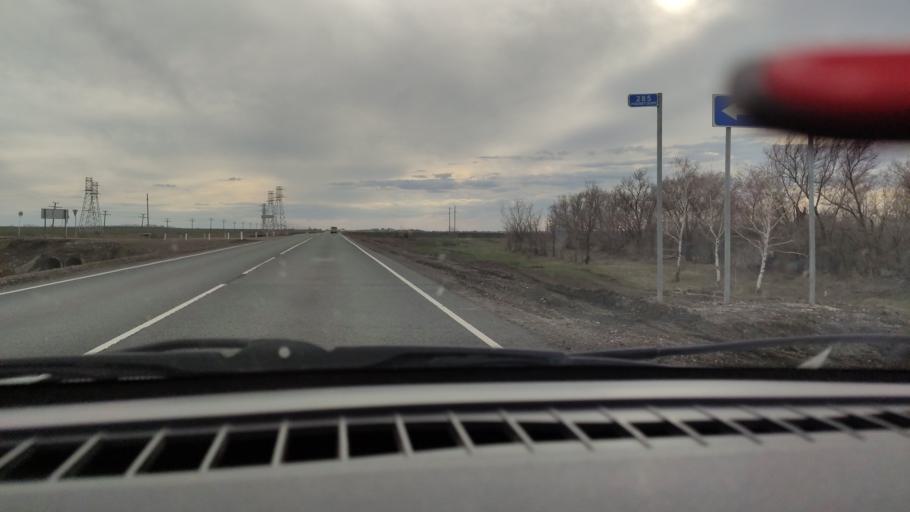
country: RU
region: Bashkortostan
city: Mayachnyy
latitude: 52.3705
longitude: 55.6190
